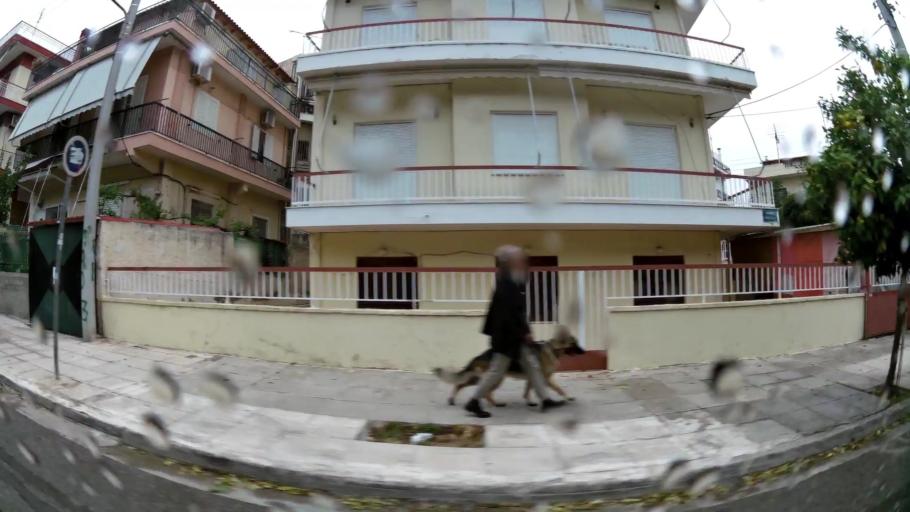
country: GR
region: Attica
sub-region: Nomarchia Athinas
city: Agia Varvara
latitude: 37.9926
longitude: 23.6660
